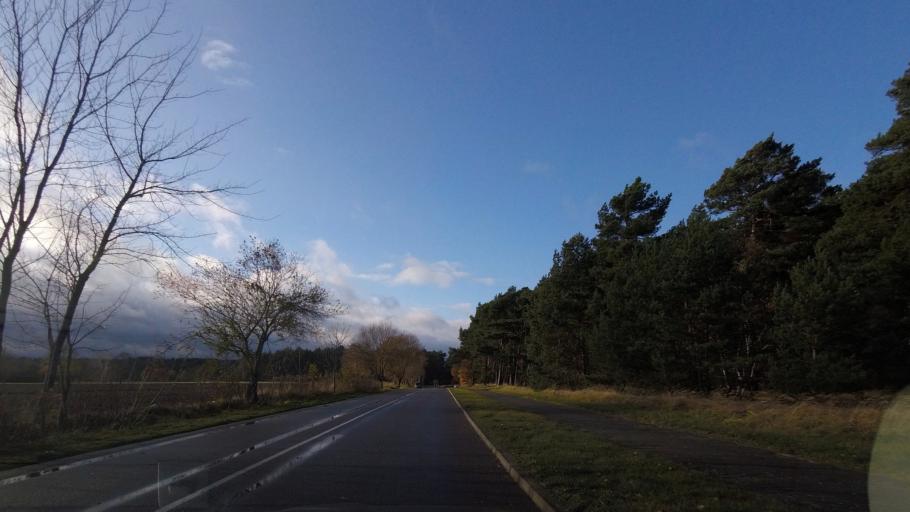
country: DE
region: Brandenburg
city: Niemegk
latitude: 52.0912
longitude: 12.6960
